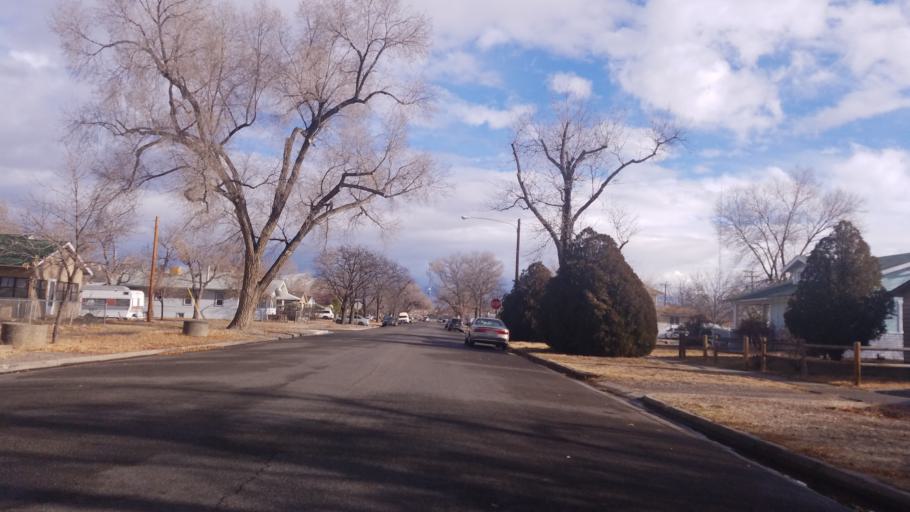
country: US
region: Colorado
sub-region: Mesa County
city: Grand Junction
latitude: 39.0663
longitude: -108.5513
